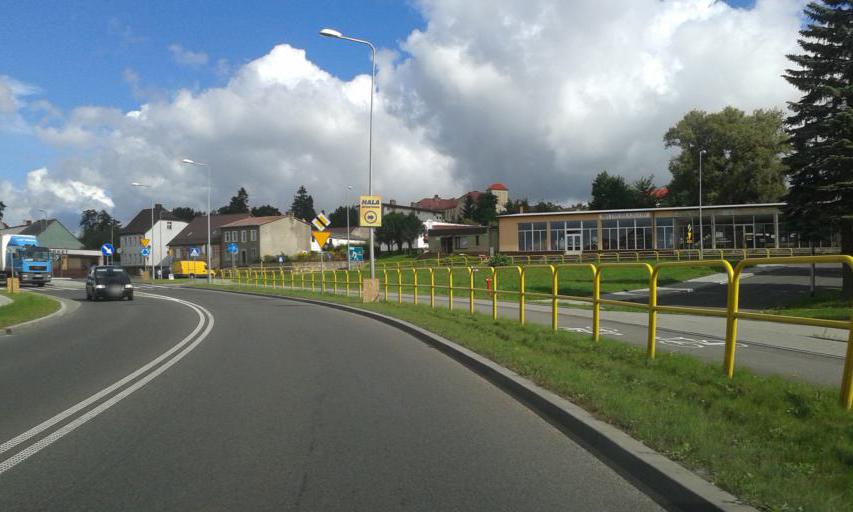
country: PL
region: West Pomeranian Voivodeship
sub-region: Powiat koszalinski
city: Bobolice
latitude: 53.9540
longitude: 16.5886
